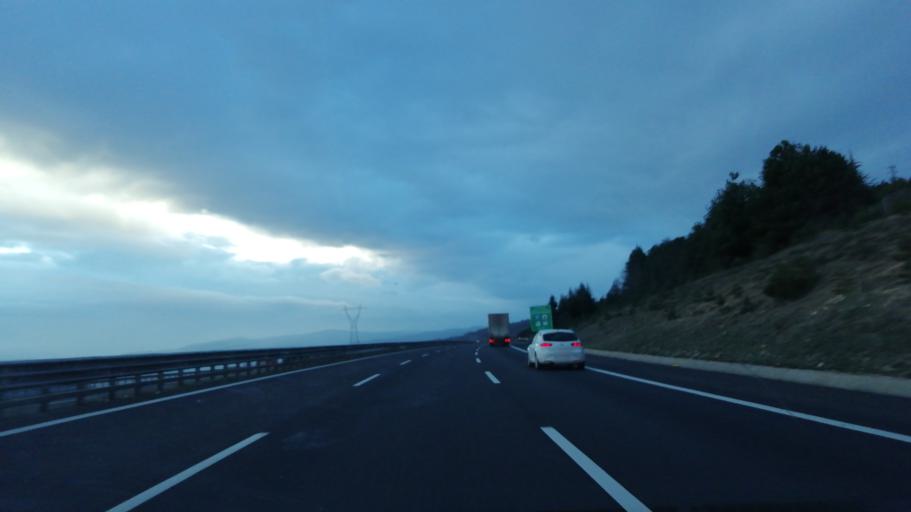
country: TR
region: Bolu
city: Bolu
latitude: 40.7362
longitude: 31.5333
